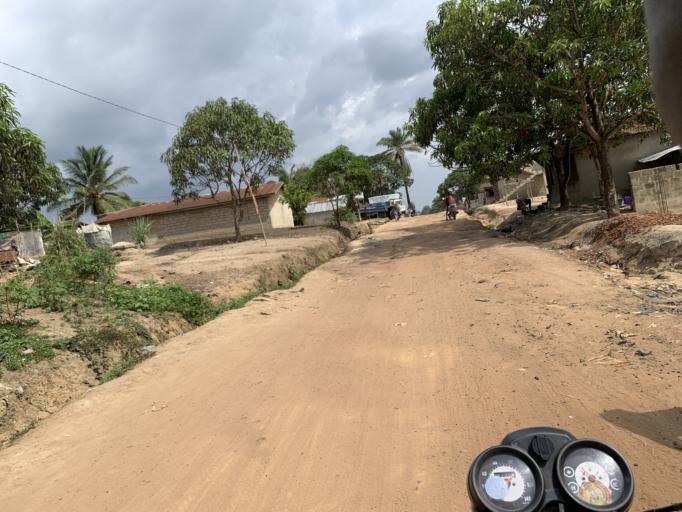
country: SL
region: Western Area
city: Waterloo
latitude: 8.3350
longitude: -13.0528
